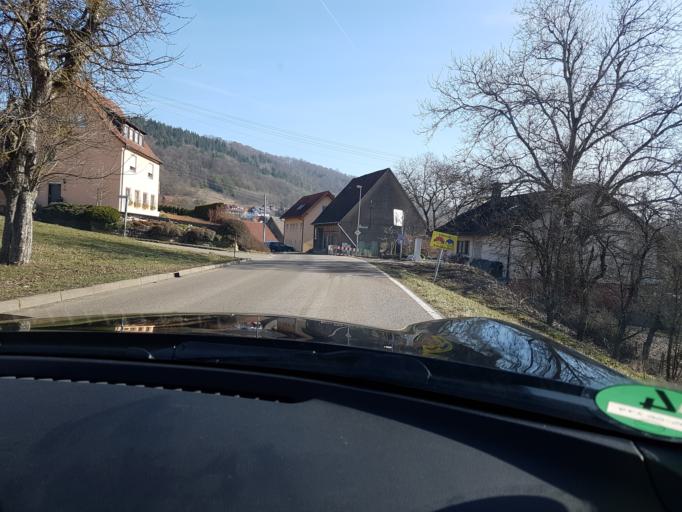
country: DE
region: Baden-Wuerttemberg
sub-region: Regierungsbezirk Stuttgart
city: Mulfingen
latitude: 49.3000
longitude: 9.8251
